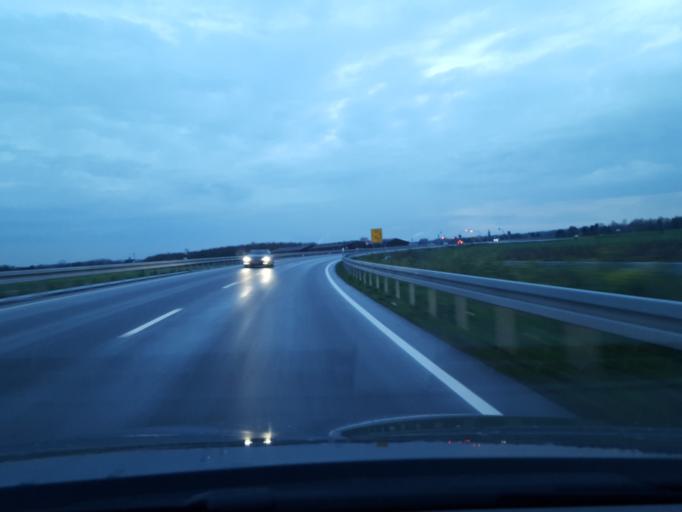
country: DE
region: North Rhine-Westphalia
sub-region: Regierungsbezirk Koln
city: Troisdorf
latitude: 50.7912
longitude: 7.1020
